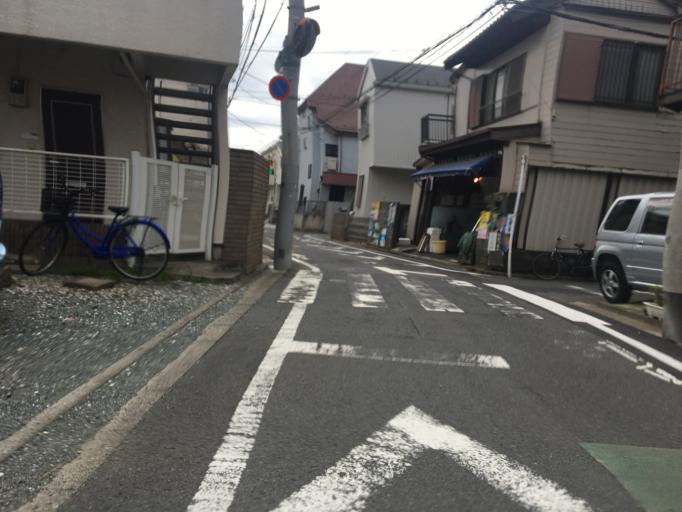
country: JP
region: Tokyo
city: Tokyo
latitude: 35.7179
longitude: 139.6469
